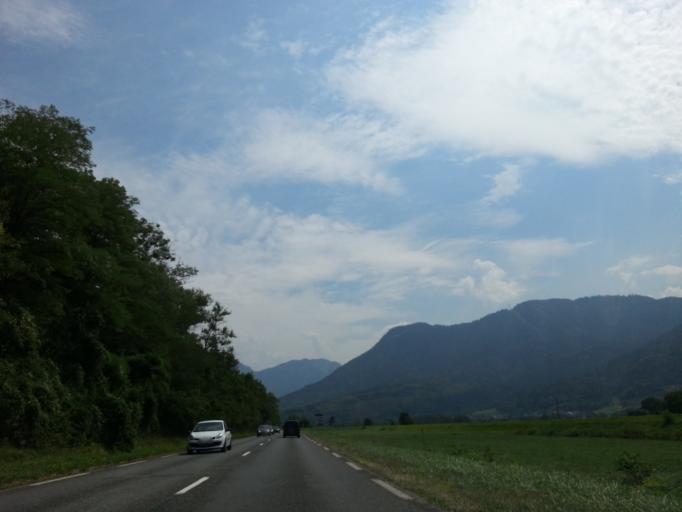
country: FR
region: Rhone-Alpes
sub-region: Departement de la Haute-Savoie
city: Doussard
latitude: 45.7691
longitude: 6.2445
